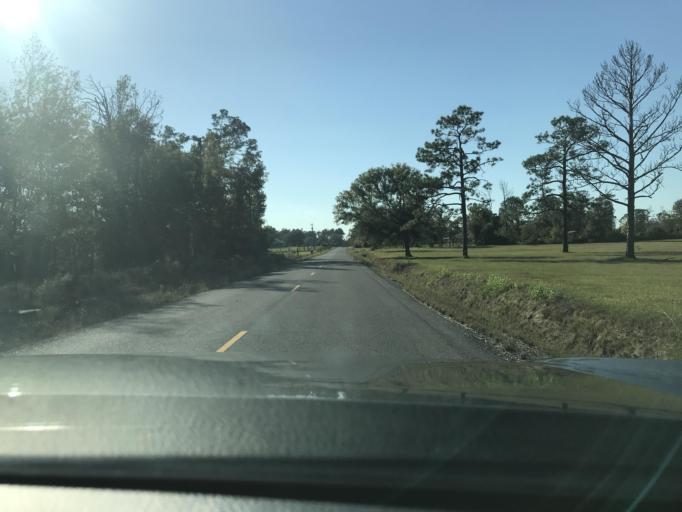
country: US
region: Louisiana
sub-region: Calcasieu Parish
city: Westlake
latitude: 30.3153
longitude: -93.2648
